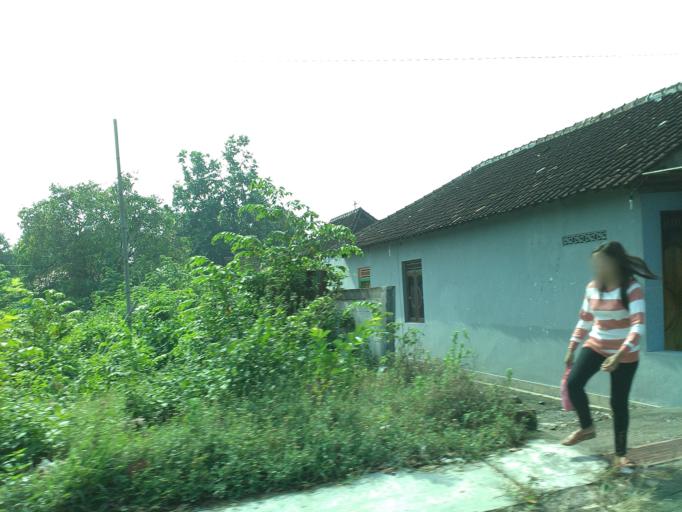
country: ID
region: Central Java
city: Ceper
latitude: -7.6520
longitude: 110.6831
